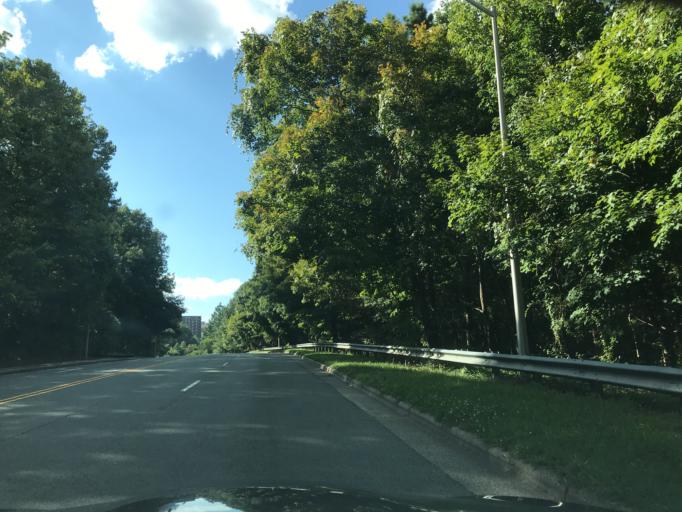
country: US
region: North Carolina
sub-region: Orange County
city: Chapel Hill
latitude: 35.8998
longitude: -79.0378
